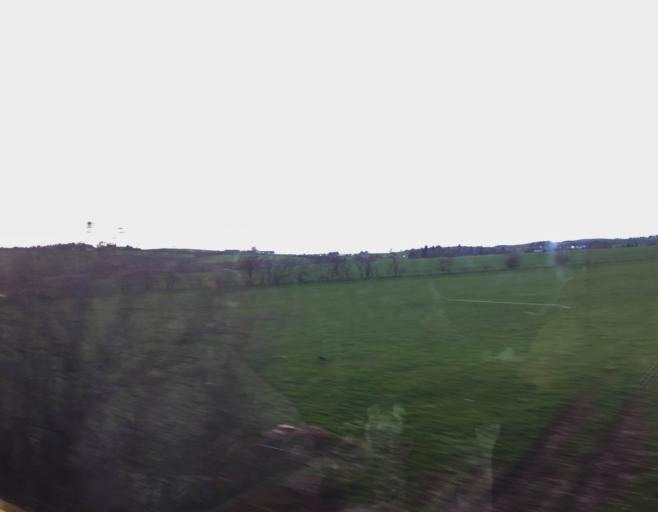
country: GB
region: Scotland
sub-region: Dumfries and Galloway
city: Lockerbie
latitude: 55.0658
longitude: -3.2934
